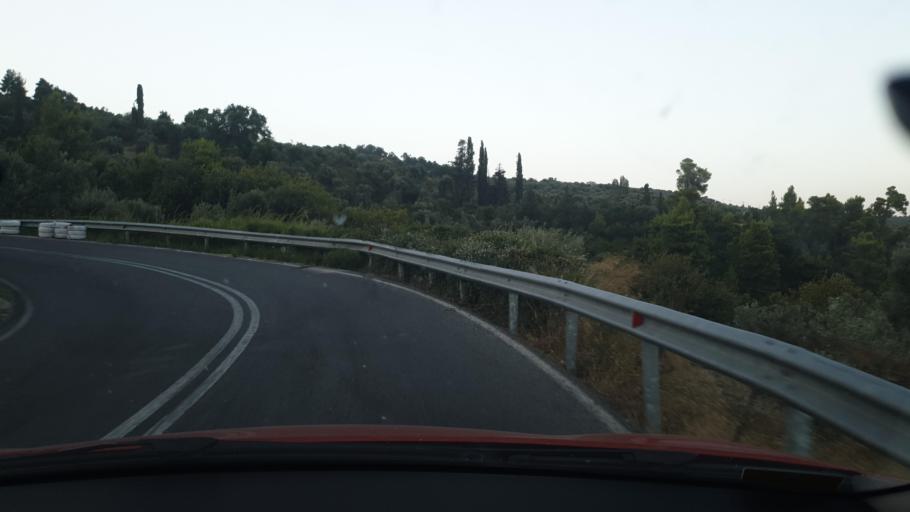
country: GR
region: Central Greece
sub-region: Nomos Evvoias
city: Kymi
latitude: 38.6318
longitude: 24.1168
